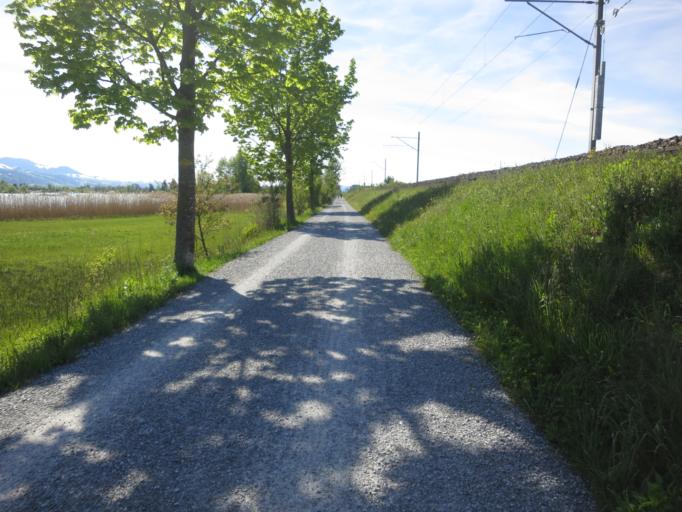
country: CH
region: Saint Gallen
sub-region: Wahlkreis See-Gaster
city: Jona
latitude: 47.2222
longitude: 8.8605
